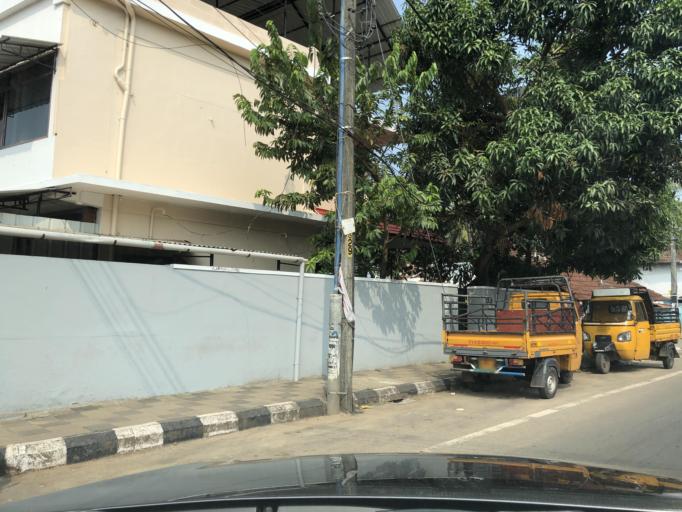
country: IN
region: Kerala
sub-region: Kozhikode
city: Kozhikode
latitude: 11.2636
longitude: 75.7699
